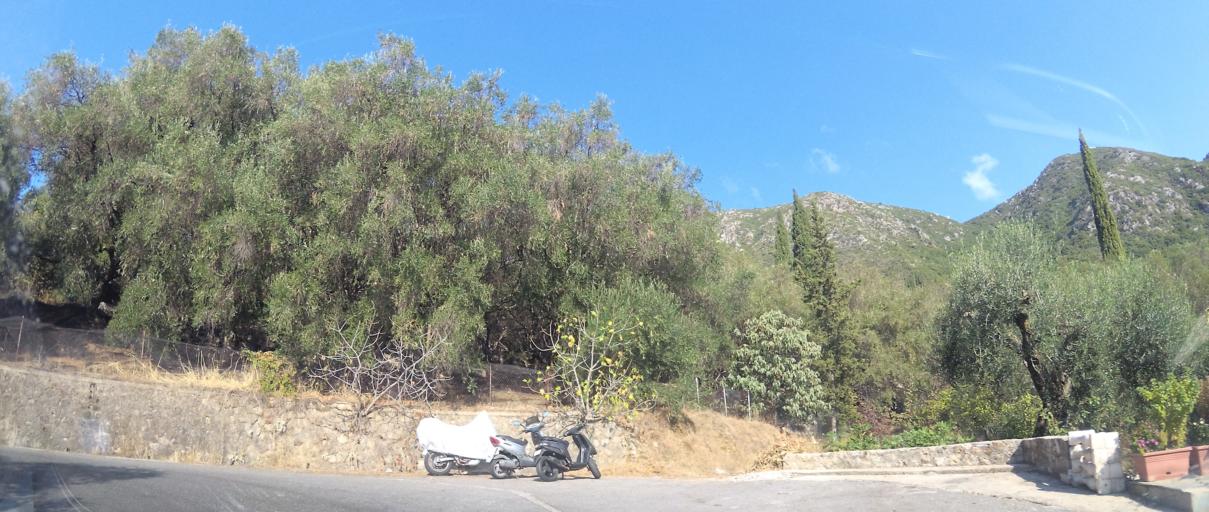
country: GR
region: Ionian Islands
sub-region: Nomos Kerkyras
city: Kontokali
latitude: 39.7196
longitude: 19.8477
